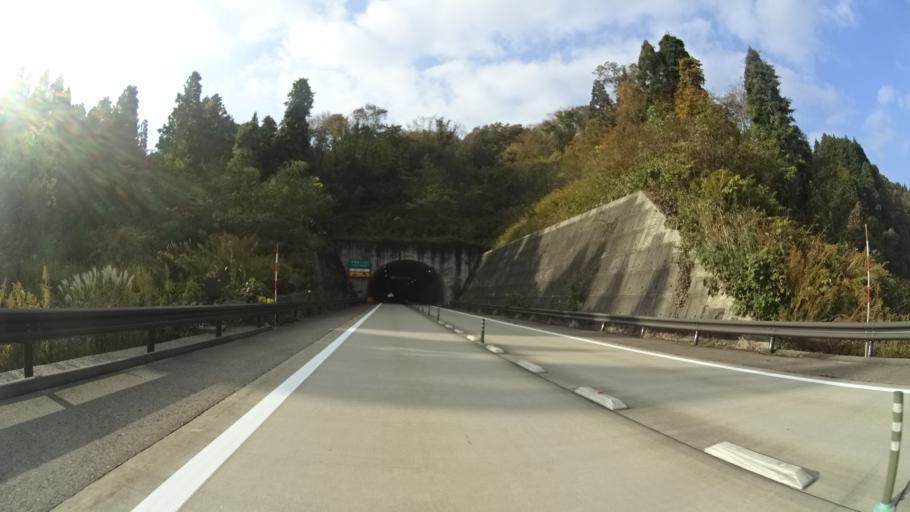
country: JP
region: Toyama
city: Himi
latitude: 36.9305
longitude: 137.0129
